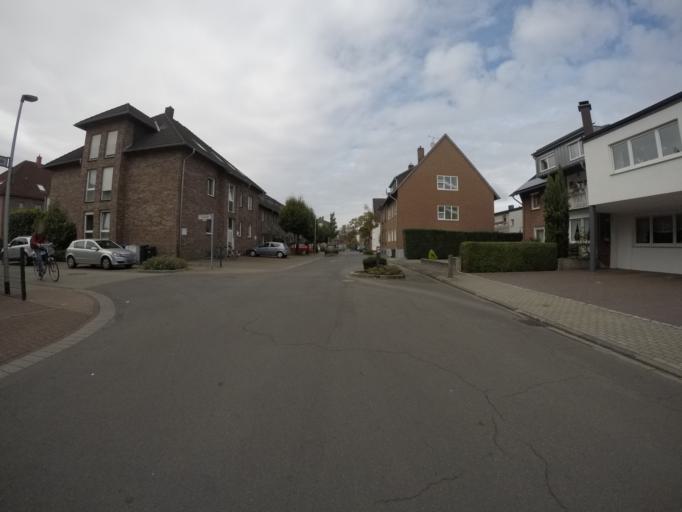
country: DE
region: North Rhine-Westphalia
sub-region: Regierungsbezirk Dusseldorf
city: Bocholt
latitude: 51.8389
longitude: 6.6343
